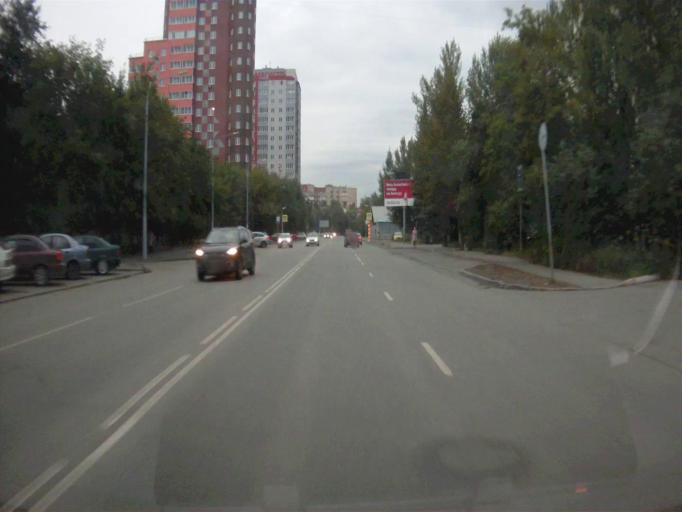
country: RU
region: Chelyabinsk
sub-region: Gorod Chelyabinsk
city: Chelyabinsk
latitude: 55.1505
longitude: 61.3985
